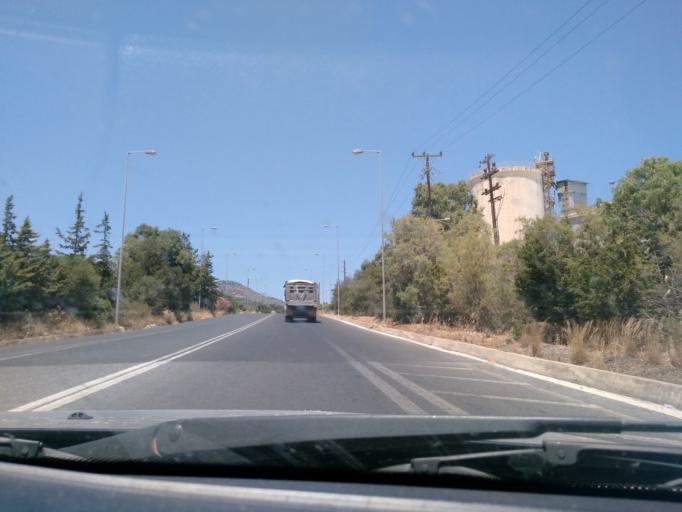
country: GR
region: Crete
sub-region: Nomos Irakleiou
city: Gazi
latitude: 35.3449
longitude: 25.0458
